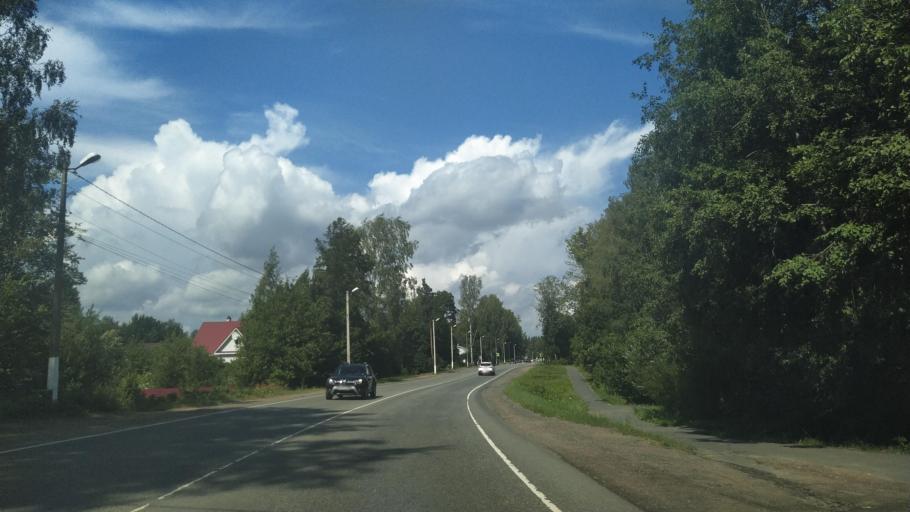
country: RU
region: Leningrad
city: Toksovo
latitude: 60.1466
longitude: 30.5239
